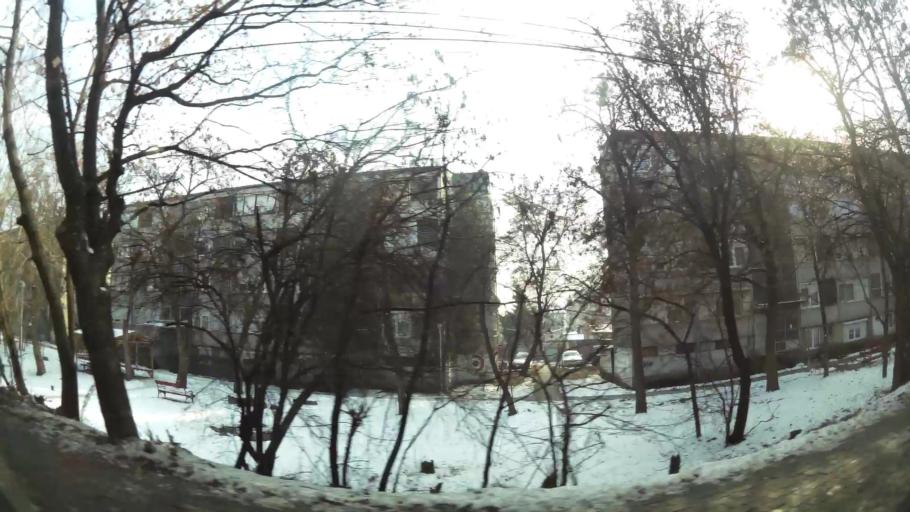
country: MK
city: Creshevo
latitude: 42.0045
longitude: 21.4985
